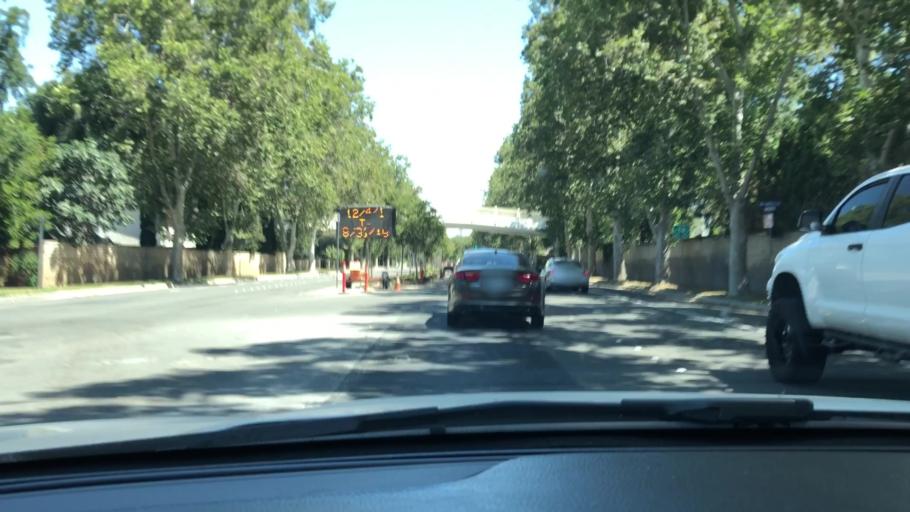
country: US
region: California
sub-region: Los Angeles County
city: Santa Clarita
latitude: 34.3945
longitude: -118.5516
